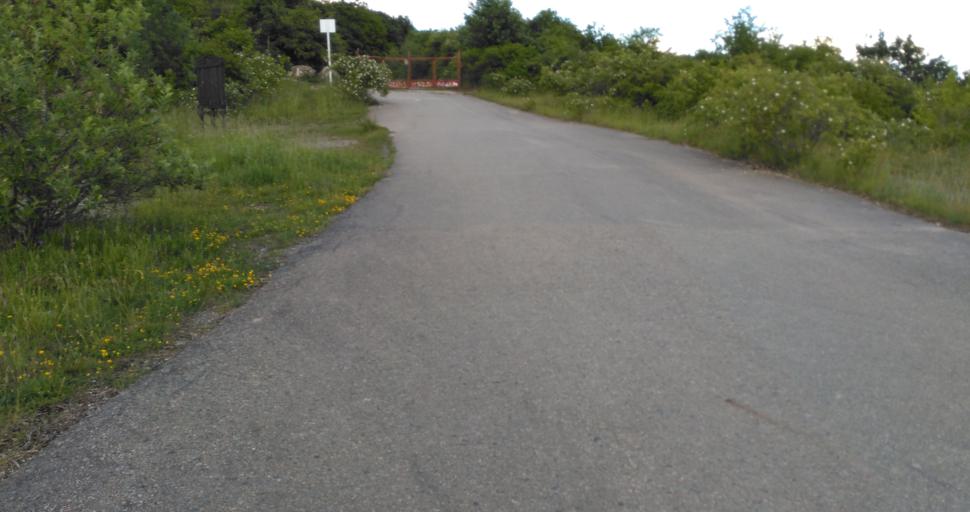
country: CZ
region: South Moravian
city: Bilovice nad Svitavou
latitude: 49.2178
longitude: 16.6757
